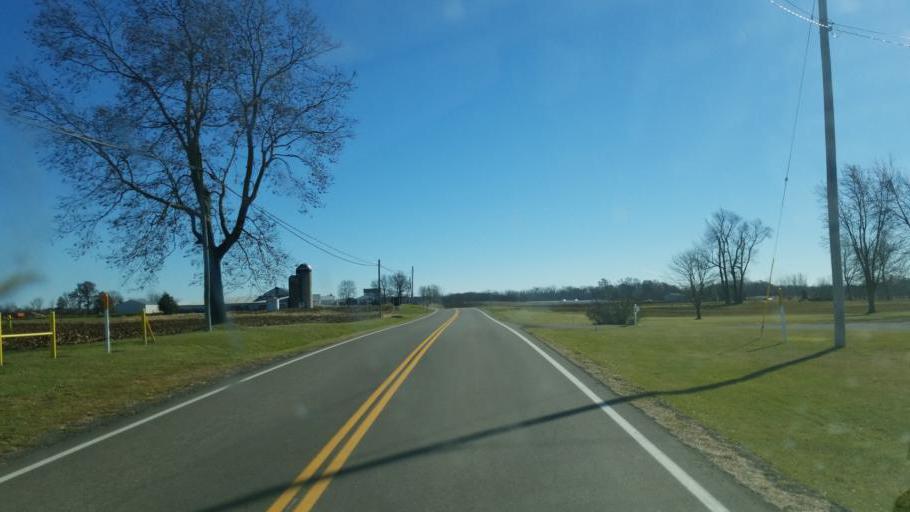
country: US
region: Ohio
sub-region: Huron County
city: Plymouth
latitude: 40.9640
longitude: -82.5951
